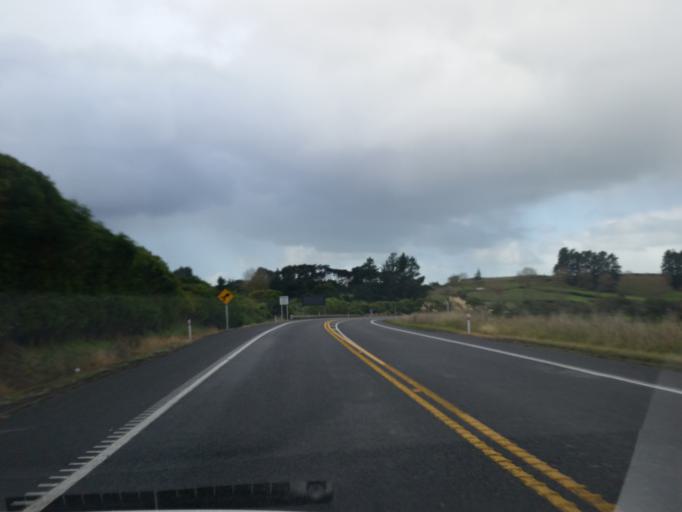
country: NZ
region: Auckland
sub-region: Auckland
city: Pukekohe East
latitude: -37.2120
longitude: 175.0757
